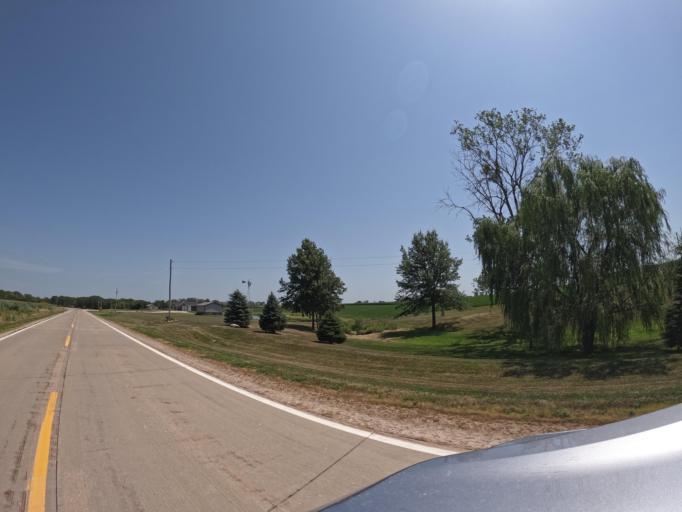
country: US
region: Iowa
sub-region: Henry County
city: Mount Pleasant
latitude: 40.9810
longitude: -91.6156
